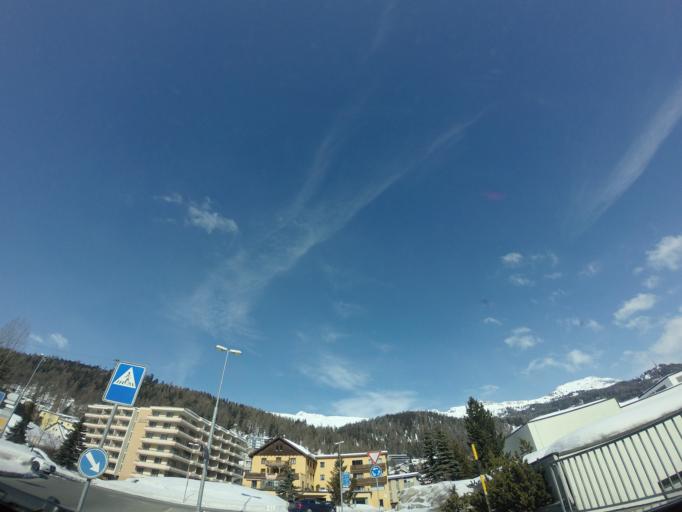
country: CH
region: Grisons
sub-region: Maloja District
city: Saint Moritz
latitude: 46.4881
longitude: 9.8367
